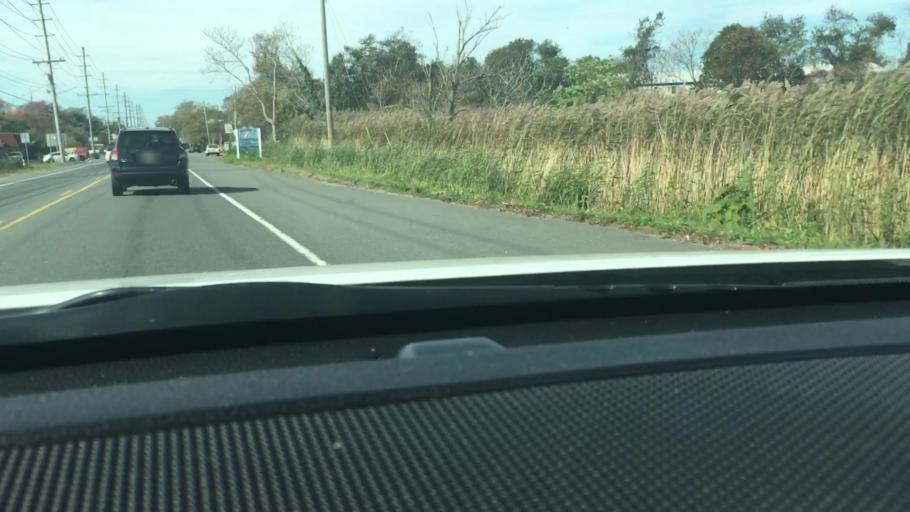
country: US
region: New Jersey
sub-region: Atlantic County
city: Pleasantville
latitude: 39.4017
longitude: -74.5056
